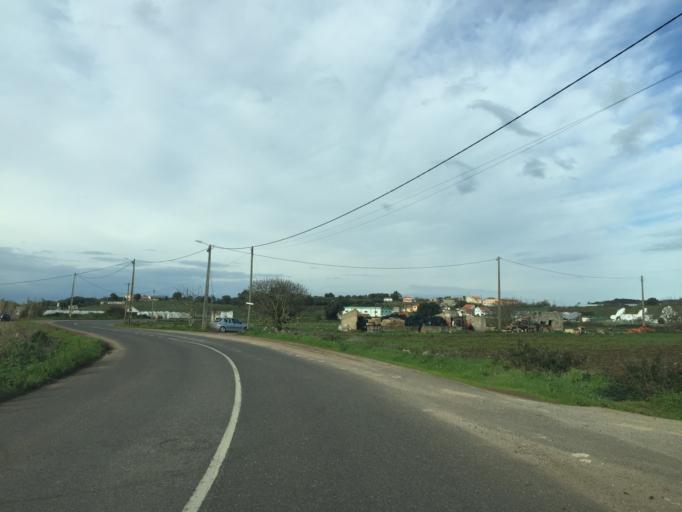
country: PT
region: Lisbon
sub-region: Sintra
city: Almargem
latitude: 38.8640
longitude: -9.2798
